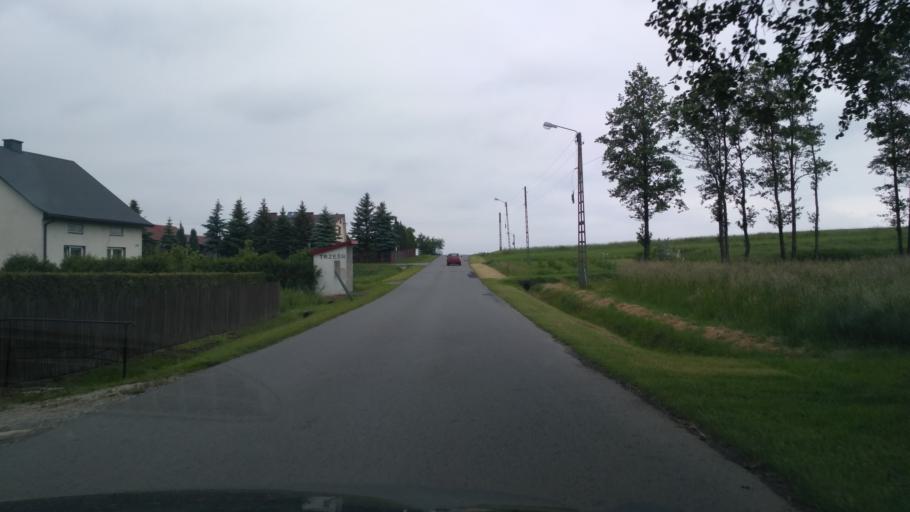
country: PL
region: Subcarpathian Voivodeship
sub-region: Powiat kolbuszowski
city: Niwiska
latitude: 50.2165
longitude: 21.6766
